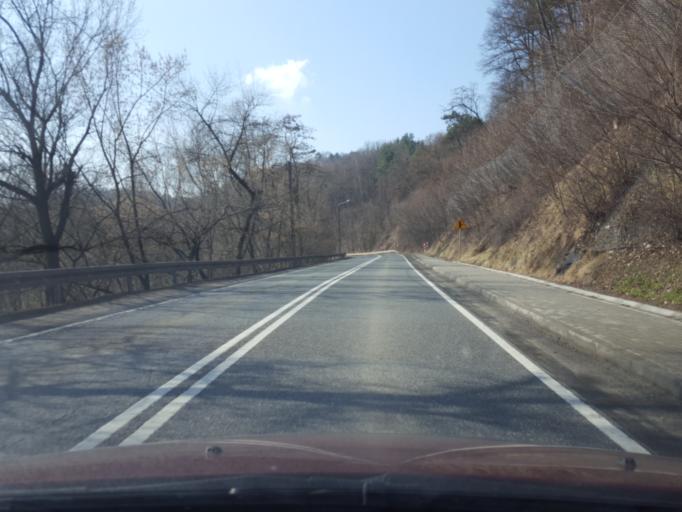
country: PL
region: Lesser Poland Voivodeship
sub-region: Powiat brzeski
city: Czchow
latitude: 49.8313
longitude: 20.6780
